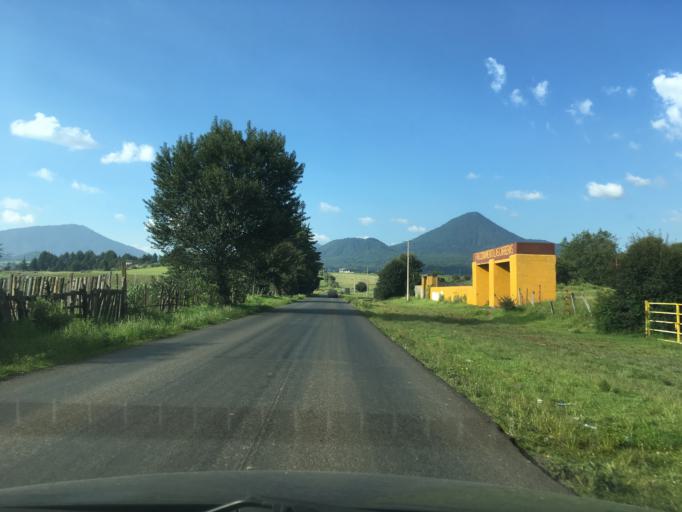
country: MX
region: Michoacan
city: Nahuatzen
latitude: 19.6424
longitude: -101.9243
